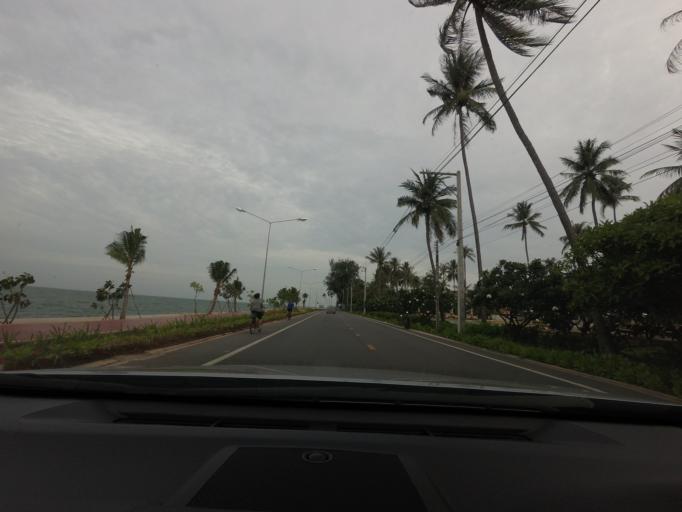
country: TH
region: Prachuap Khiri Khan
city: Pran Buri
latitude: 12.3852
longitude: 99.9990
